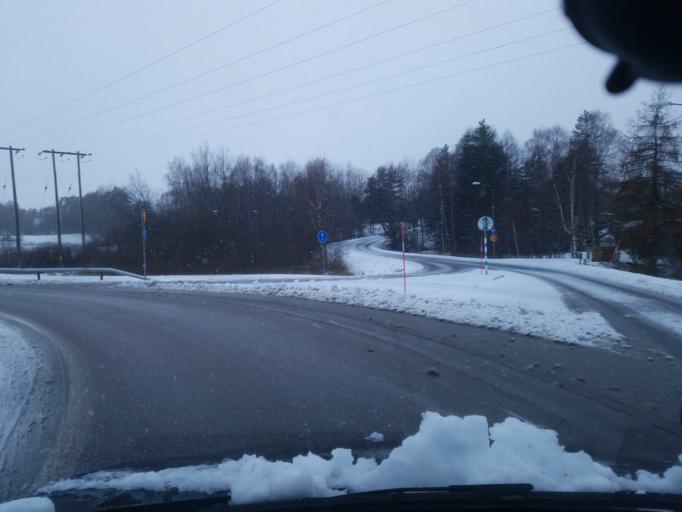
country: SE
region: Vaestra Goetaland
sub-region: Lysekils Kommun
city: Lysekil
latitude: 58.3037
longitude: 11.4759
